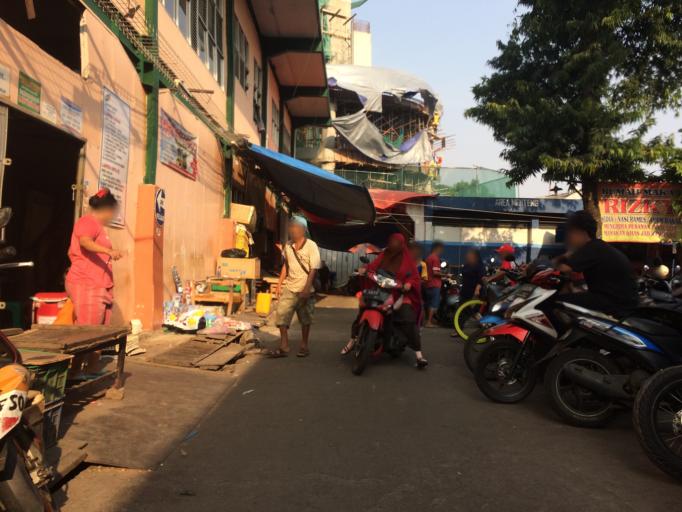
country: ID
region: Jakarta Raya
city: Jakarta
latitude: -6.2076
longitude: 106.8397
